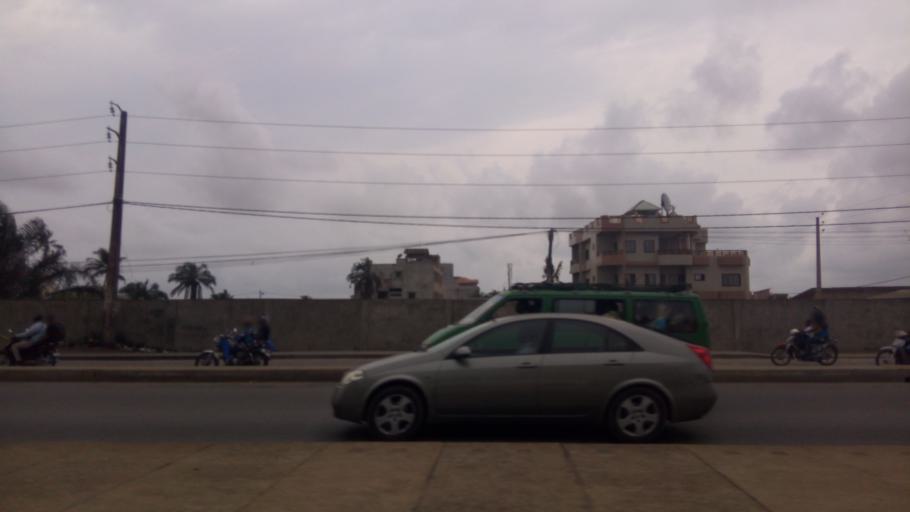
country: BJ
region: Littoral
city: Cotonou
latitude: 6.3775
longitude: 2.3835
